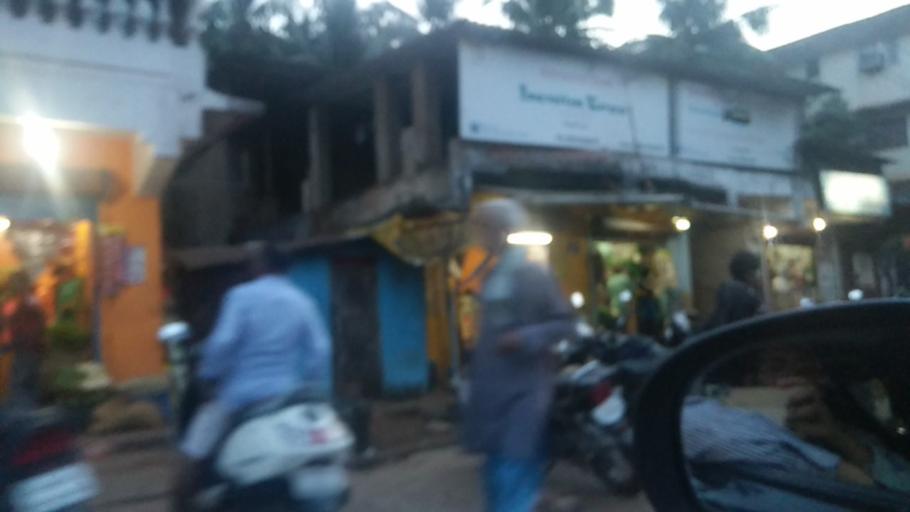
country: IN
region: Goa
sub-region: North Goa
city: Taleigao
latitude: 15.4698
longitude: 73.8219
